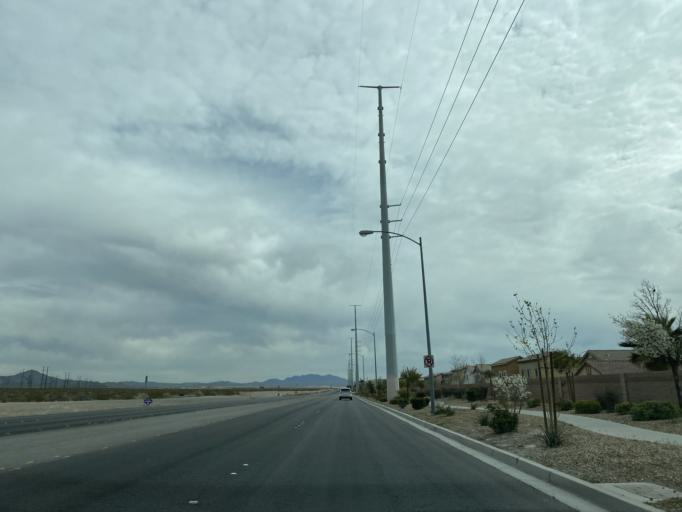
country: US
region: Nevada
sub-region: Clark County
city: Nellis Air Force Base
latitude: 36.2765
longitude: -115.0933
